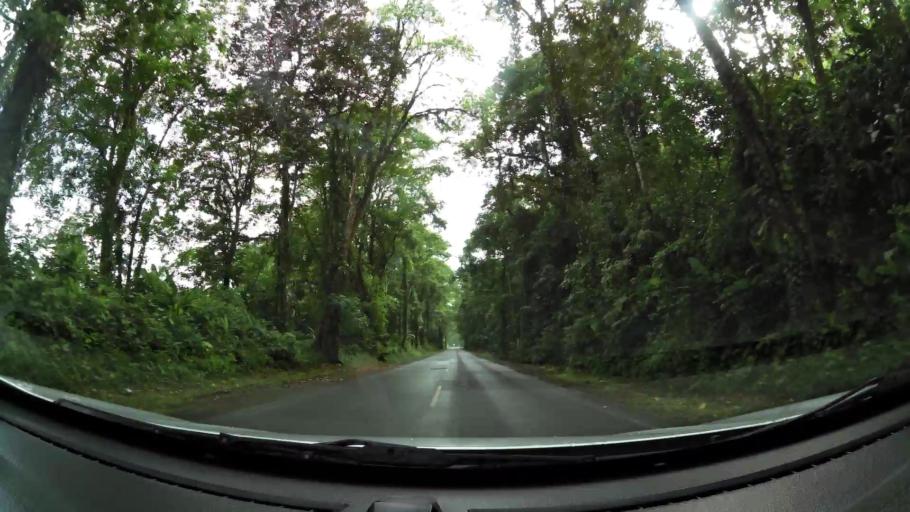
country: CR
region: Limon
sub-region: Canton de Siquirres
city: Pacuarito
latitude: 10.1014
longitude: -83.4631
